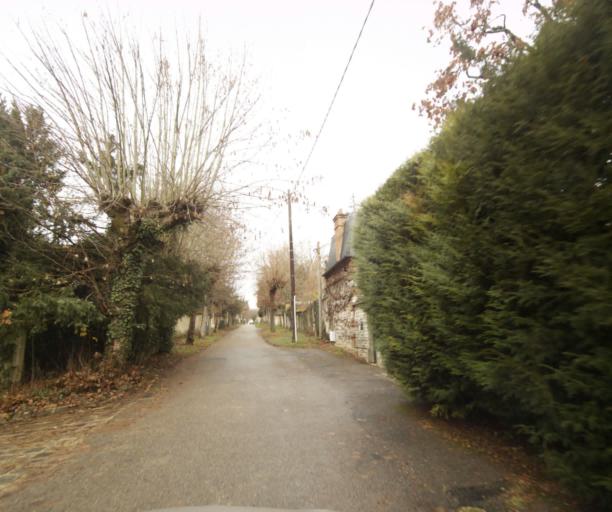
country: FR
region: Ile-de-France
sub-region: Departement de Seine-et-Marne
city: Avon
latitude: 48.4110
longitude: 2.7196
